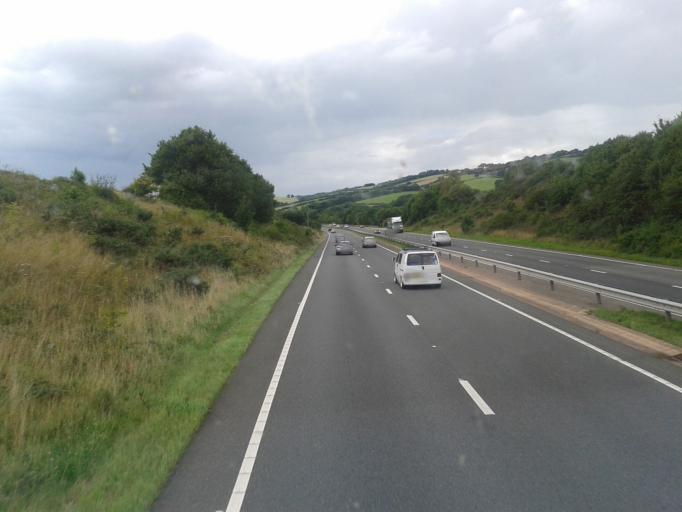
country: GB
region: England
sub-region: Devon
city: Exeter
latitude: 50.7204
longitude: -3.5996
